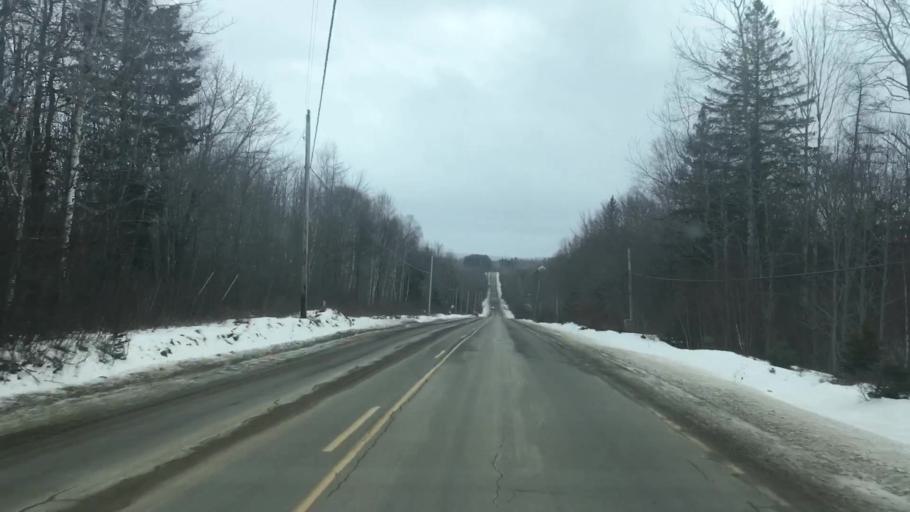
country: US
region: Maine
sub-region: Washington County
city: East Machias
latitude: 44.9714
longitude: -67.4482
